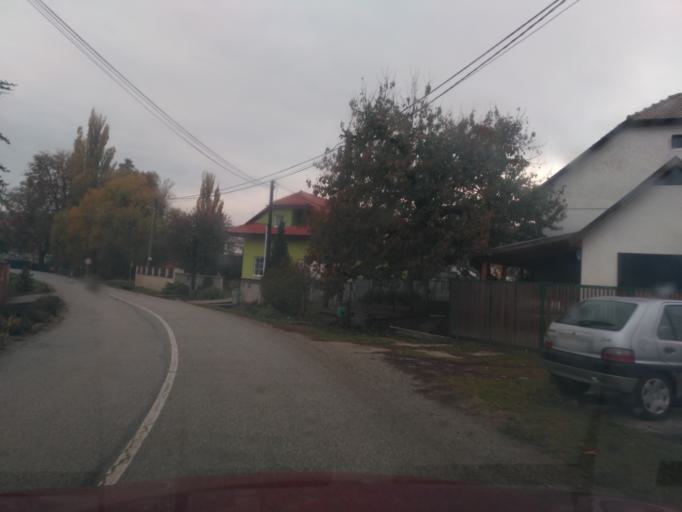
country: SK
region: Kosicky
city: Moldava nad Bodvou
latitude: 48.6746
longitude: 21.1169
